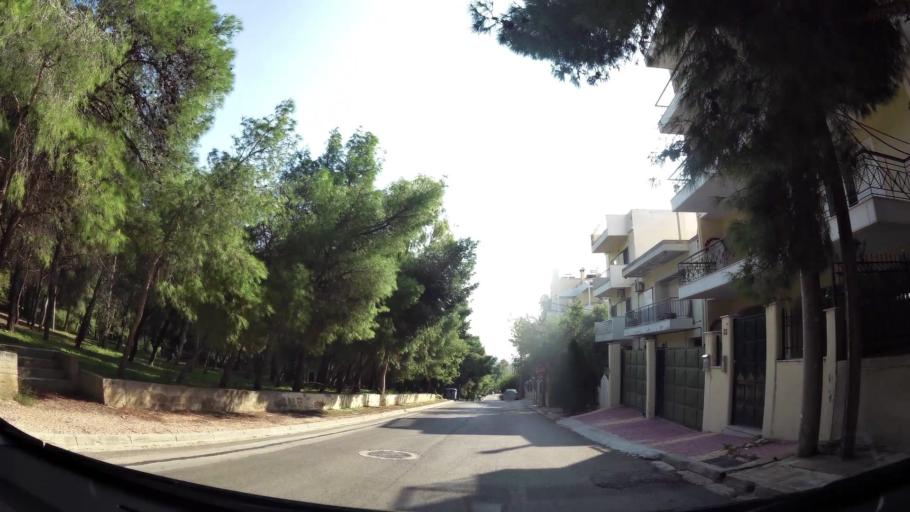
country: GR
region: Attica
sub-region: Nomarchia Athinas
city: Argyroupoli
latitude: 37.9100
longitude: 23.7592
